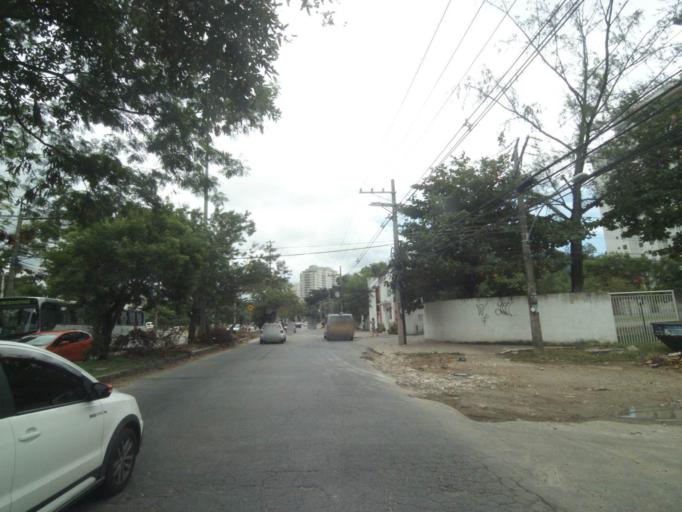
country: BR
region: Rio de Janeiro
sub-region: Nilopolis
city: Nilopolis
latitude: -22.9657
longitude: -43.4098
